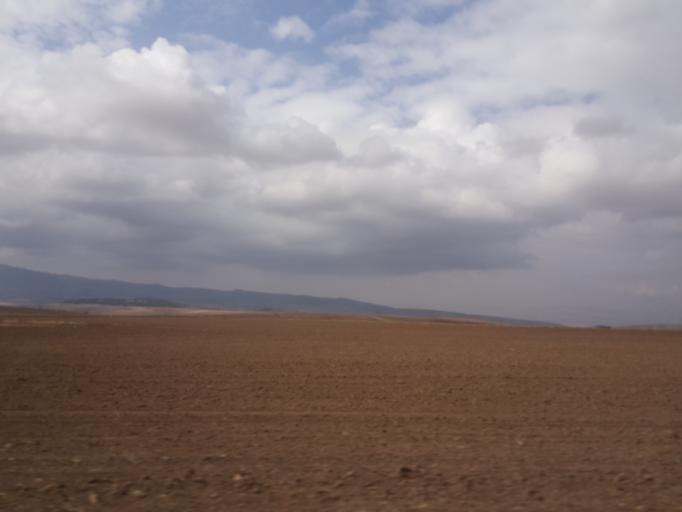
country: TR
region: Kirikkale
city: Keskin
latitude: 39.6220
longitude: 33.6122
